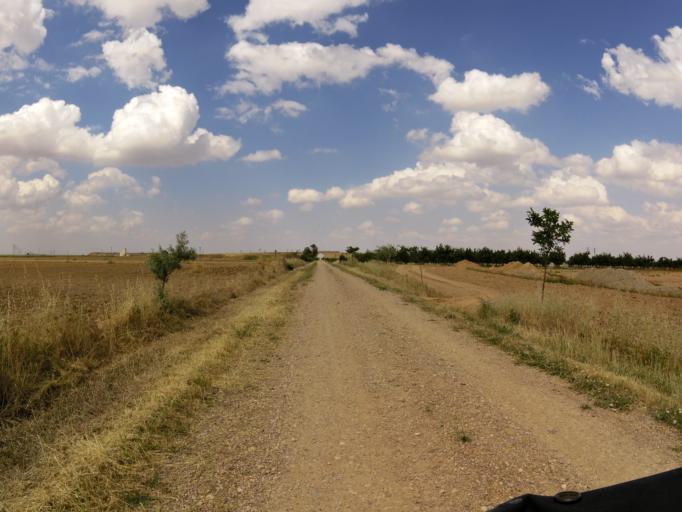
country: ES
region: Castille-La Mancha
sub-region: Provincia de Albacete
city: Albacete
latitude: 38.9286
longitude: -1.9963
